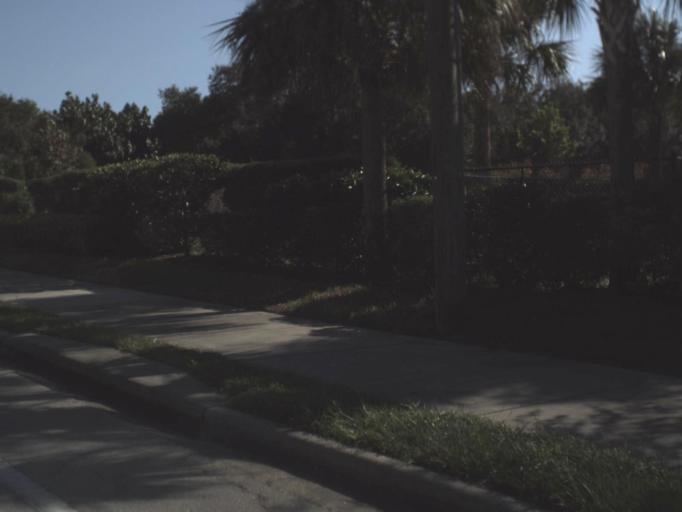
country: US
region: Florida
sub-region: Sarasota County
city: Englewood
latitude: 27.0097
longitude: -82.3824
